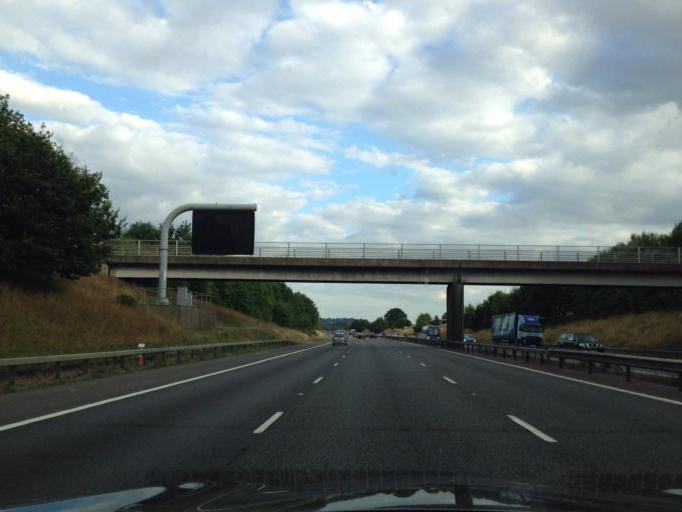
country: GB
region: England
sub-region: Oxfordshire
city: Adderbury
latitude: 52.0216
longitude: -1.2920
